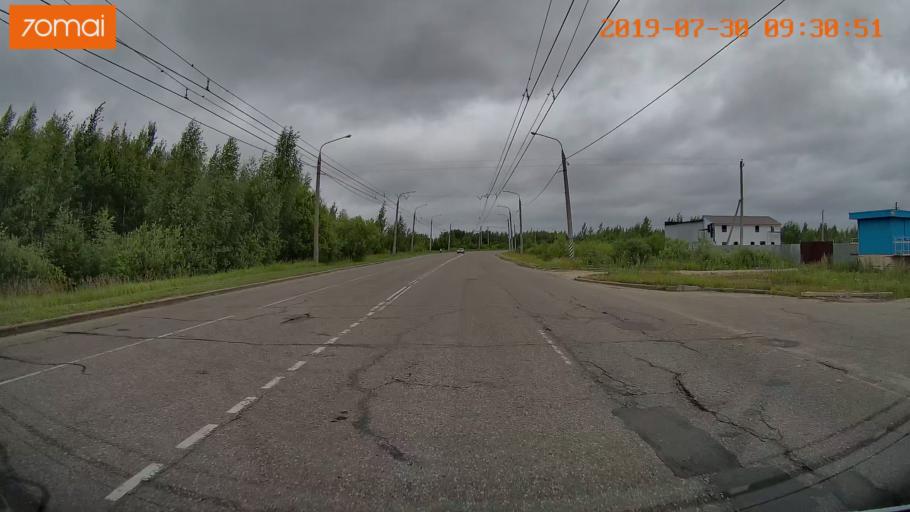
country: RU
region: Ivanovo
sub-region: Gorod Ivanovo
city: Ivanovo
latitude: 56.9497
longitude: 40.9474
